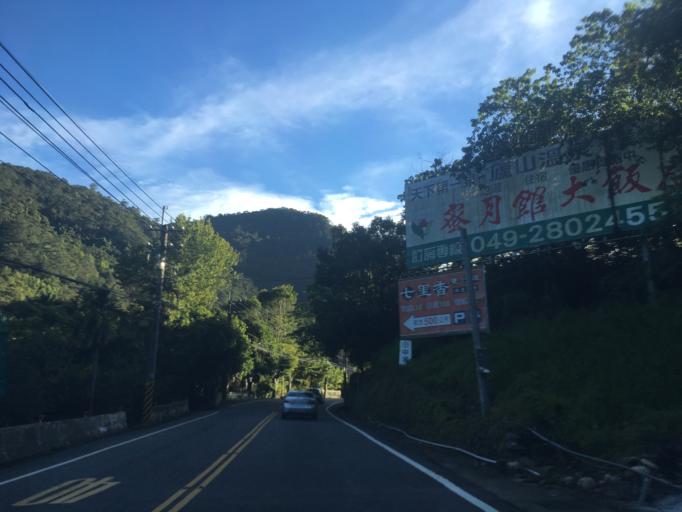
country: TW
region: Taiwan
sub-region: Nantou
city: Puli
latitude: 23.9984
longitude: 121.0801
